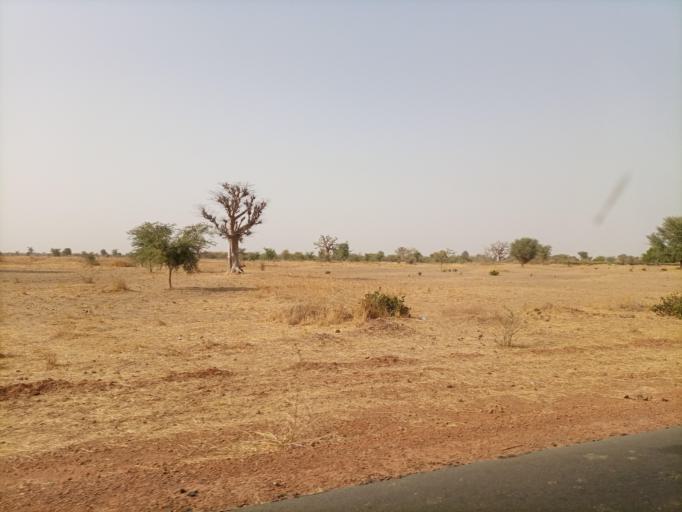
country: SN
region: Fatick
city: Foundiougne
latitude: 14.1280
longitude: -16.4119
